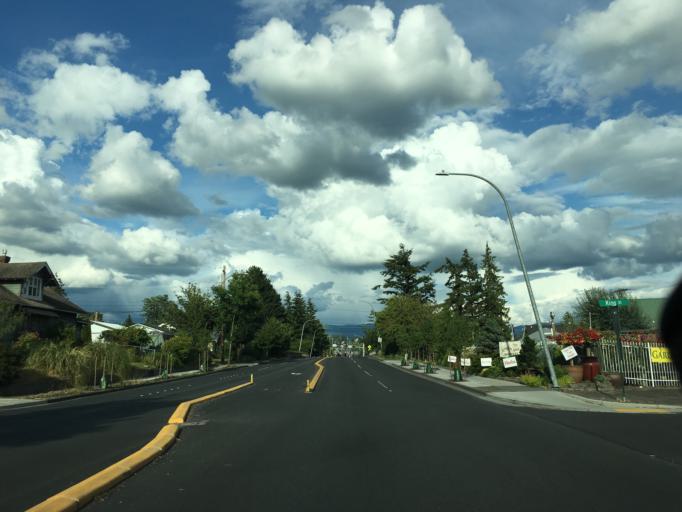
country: US
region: Washington
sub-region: Whatcom County
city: Bellingham
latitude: 48.7630
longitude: -122.4637
